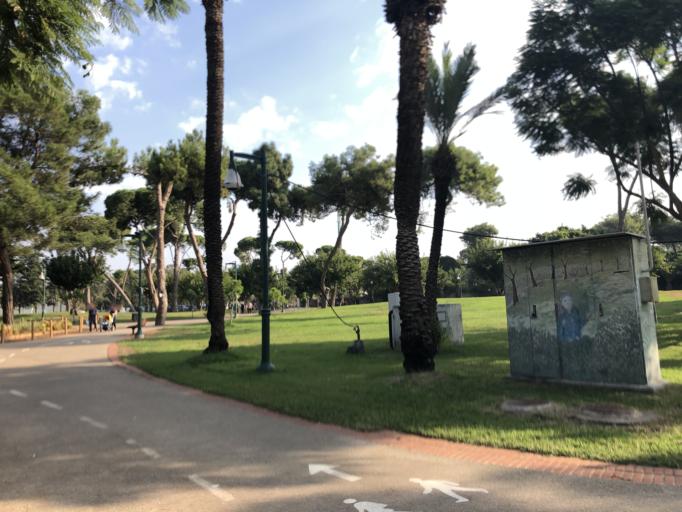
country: IL
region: Tel Aviv
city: Giv`atayim
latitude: 32.0509
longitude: 34.8273
